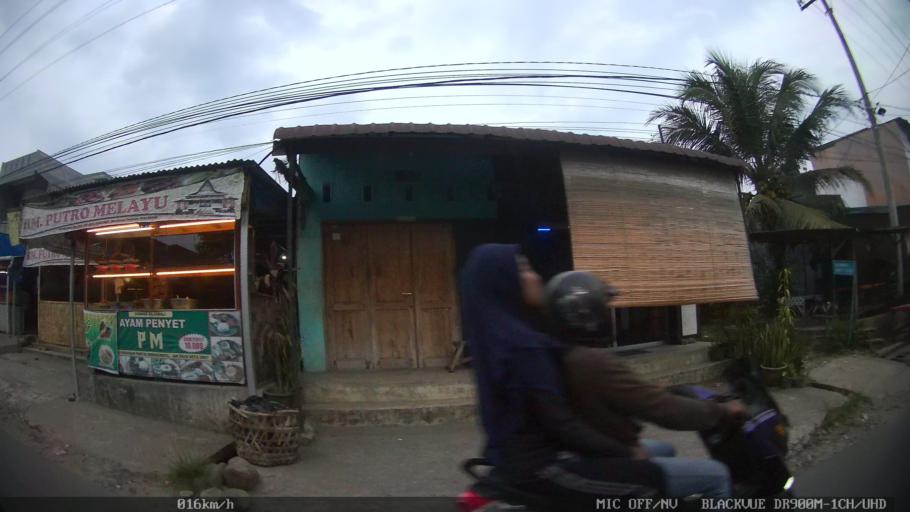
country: ID
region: North Sumatra
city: Sunggal
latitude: 3.5771
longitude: 98.5888
